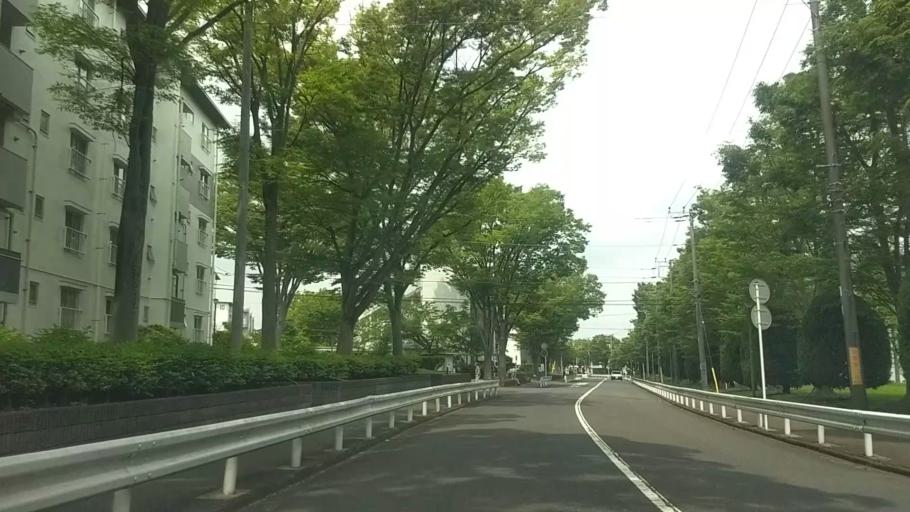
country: JP
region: Kanagawa
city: Fujisawa
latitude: 35.3659
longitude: 139.4673
